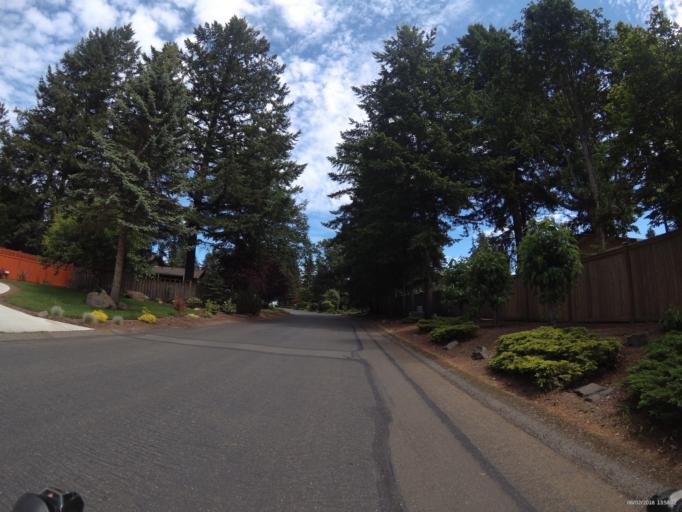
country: US
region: Washington
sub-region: Pierce County
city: University Place
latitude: 47.2088
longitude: -122.5664
